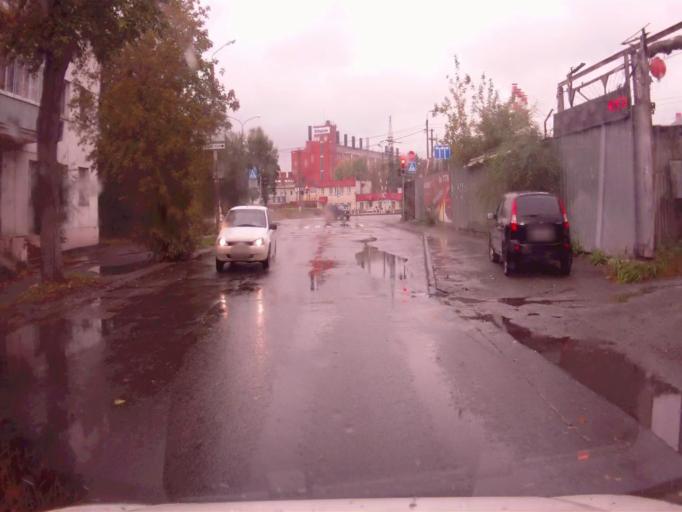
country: RU
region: Chelyabinsk
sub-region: Gorod Chelyabinsk
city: Chelyabinsk
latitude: 55.1981
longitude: 61.4070
